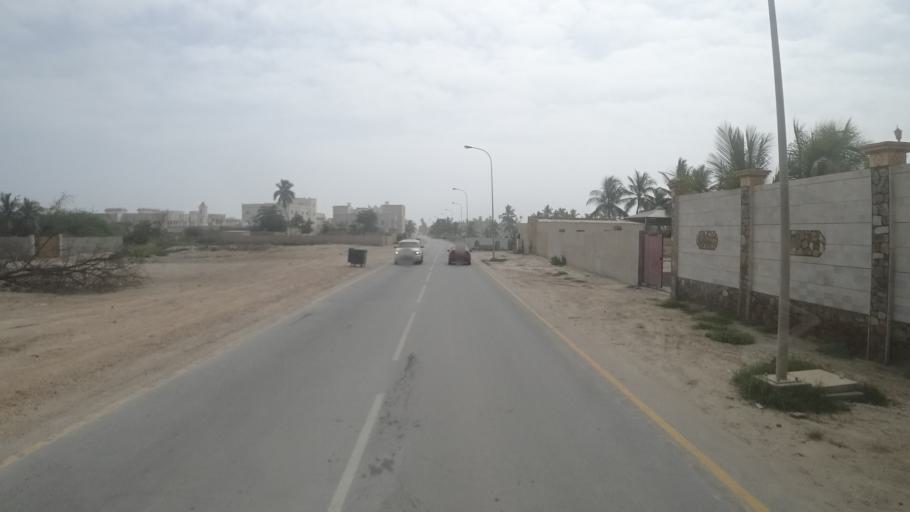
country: OM
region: Zufar
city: Salalah
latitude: 17.0128
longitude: 54.1650
